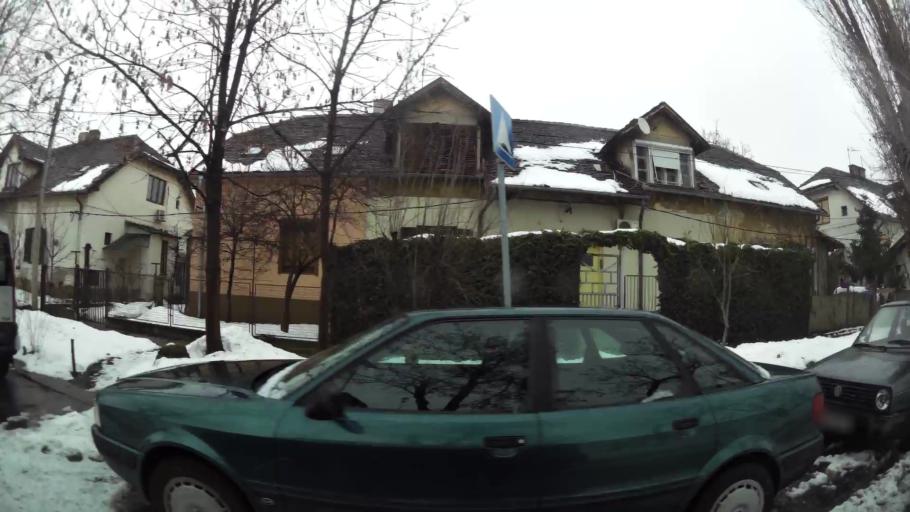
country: RS
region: Central Serbia
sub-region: Belgrade
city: Zemun
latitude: 44.8368
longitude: 20.3727
